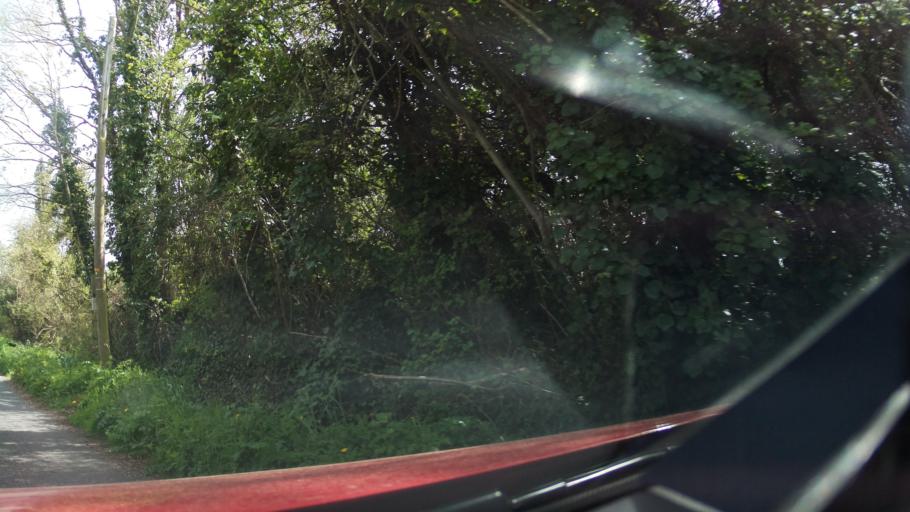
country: GB
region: England
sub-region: Hampshire
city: Romsey
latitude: 51.0333
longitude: -1.5067
